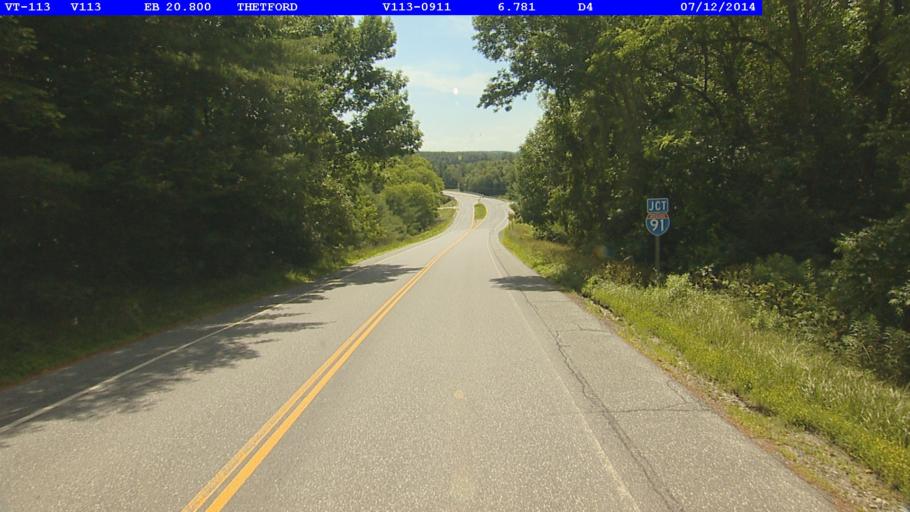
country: US
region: New Hampshire
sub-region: Grafton County
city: Lyme
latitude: 43.8148
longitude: -72.2202
